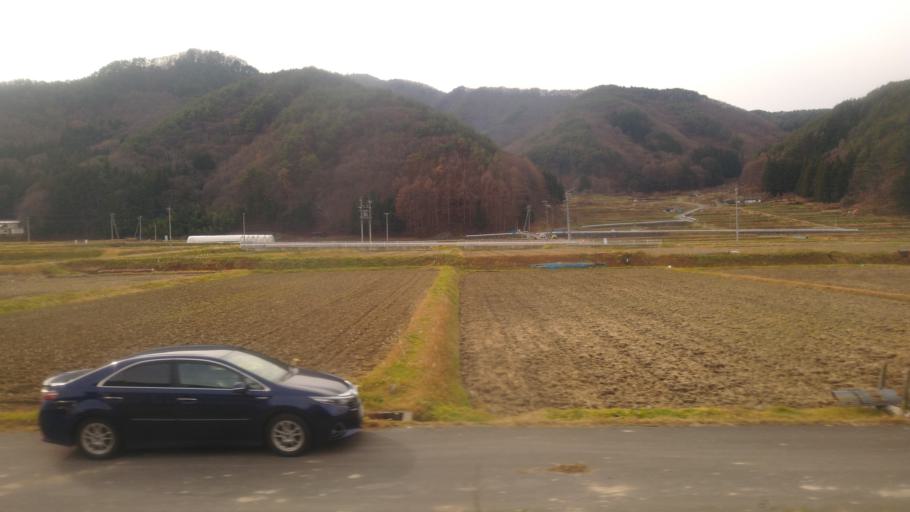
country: JP
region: Nagano
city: Omachi
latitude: 36.4524
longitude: 138.0629
